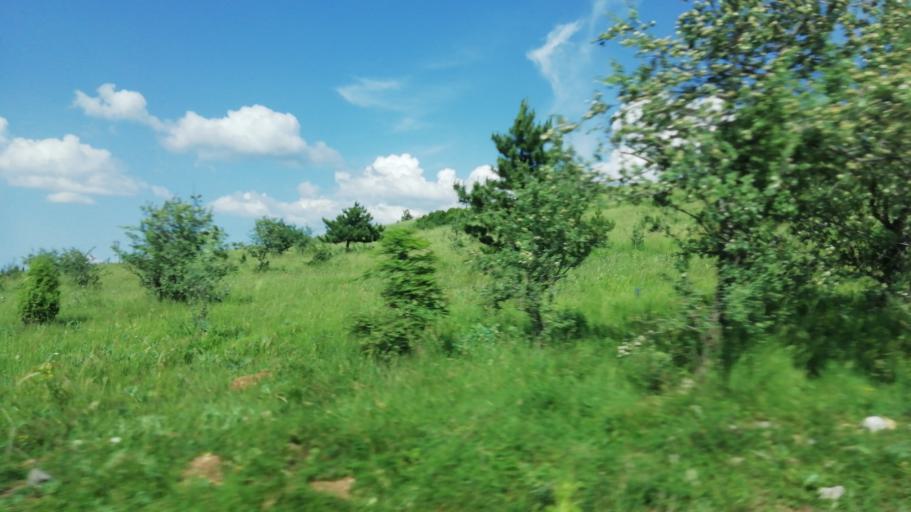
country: TR
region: Karabuk
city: Karabuk
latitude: 41.1269
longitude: 32.5757
